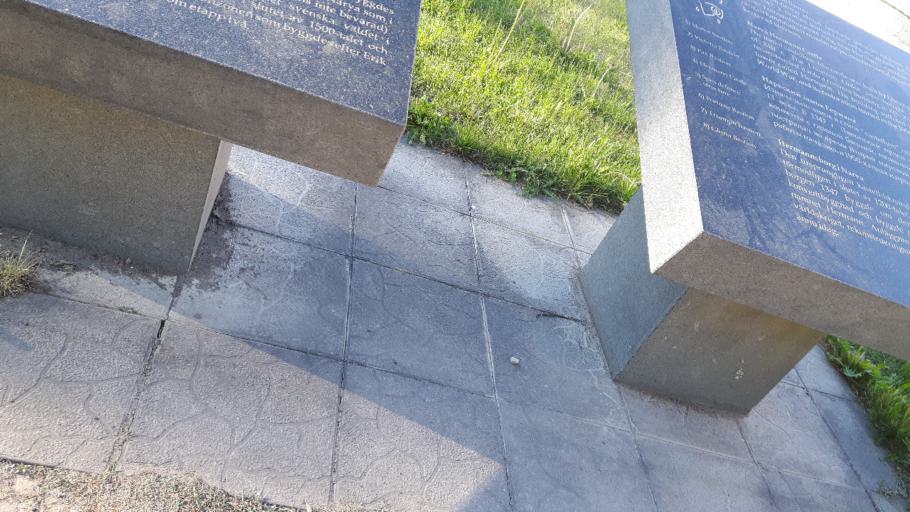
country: EE
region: Ida-Virumaa
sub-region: Narva linn
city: Narva
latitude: 59.3756
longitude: 28.1986
